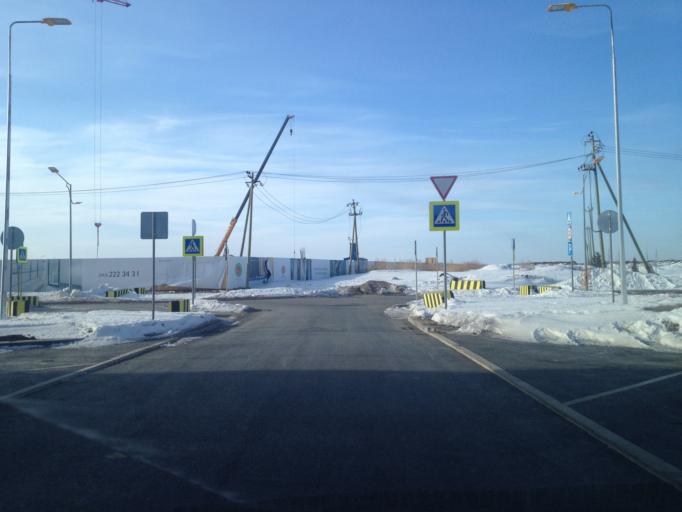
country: RU
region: Sverdlovsk
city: Sovkhoznyy
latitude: 56.7467
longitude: 60.5664
